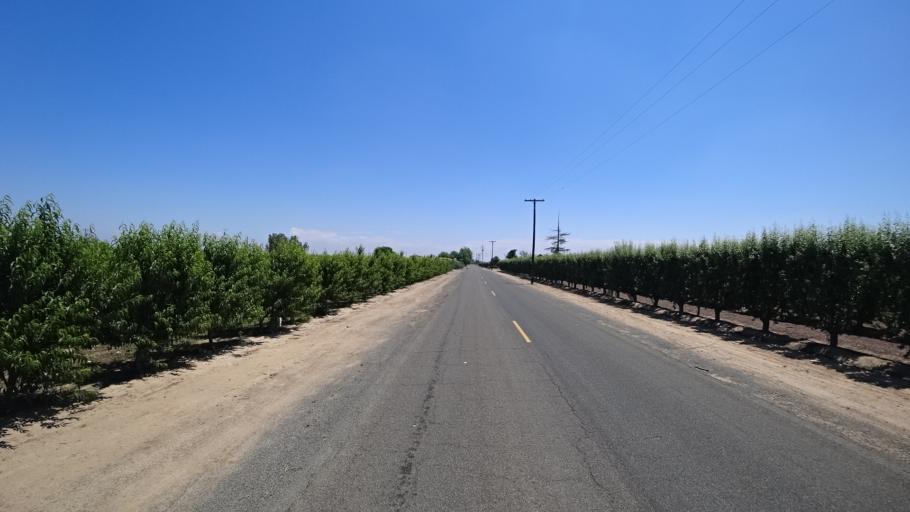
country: US
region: California
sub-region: Fresno County
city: Kingsburg
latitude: 36.4742
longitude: -119.5879
